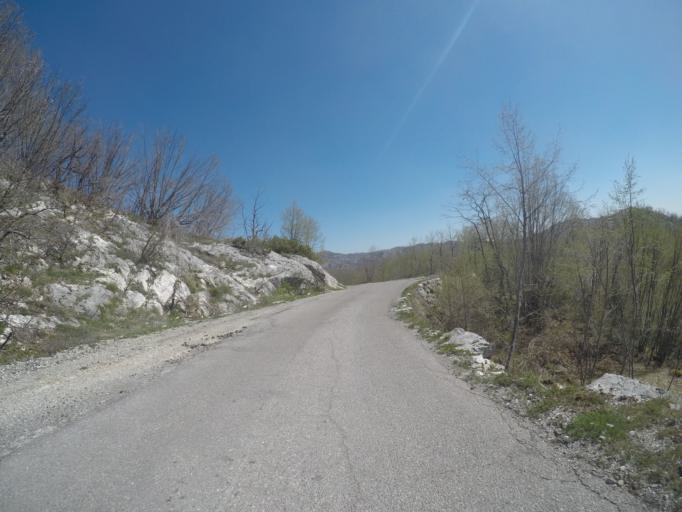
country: ME
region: Cetinje
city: Cetinje
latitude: 42.4356
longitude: 18.8686
